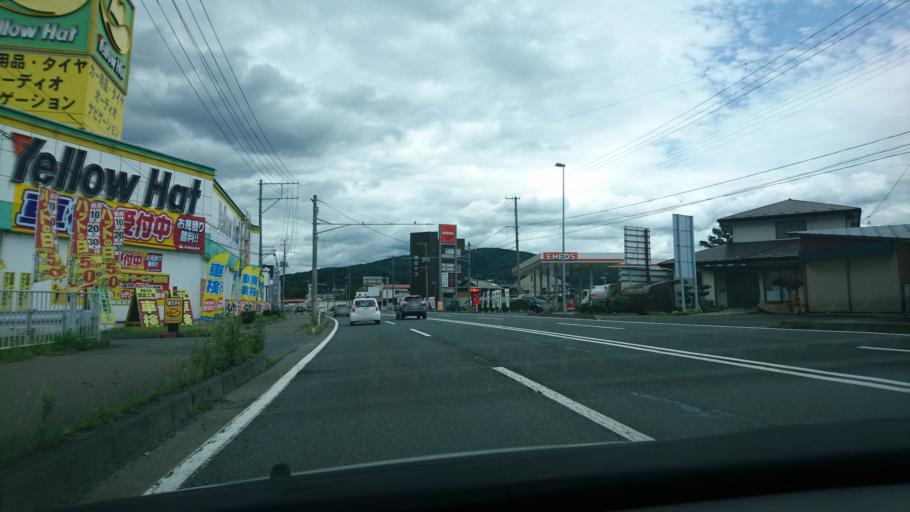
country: JP
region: Iwate
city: Morioka-shi
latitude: 39.6867
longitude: 141.1636
